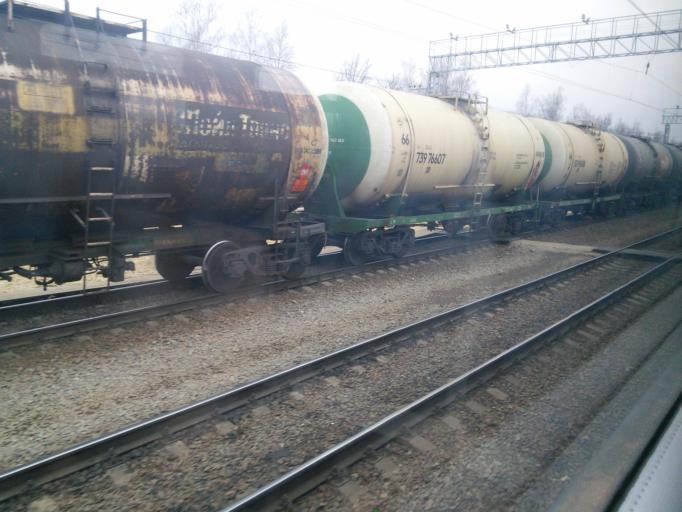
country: RU
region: Moskovskaya
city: Yakovlevskoye
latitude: 55.4276
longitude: 37.8825
